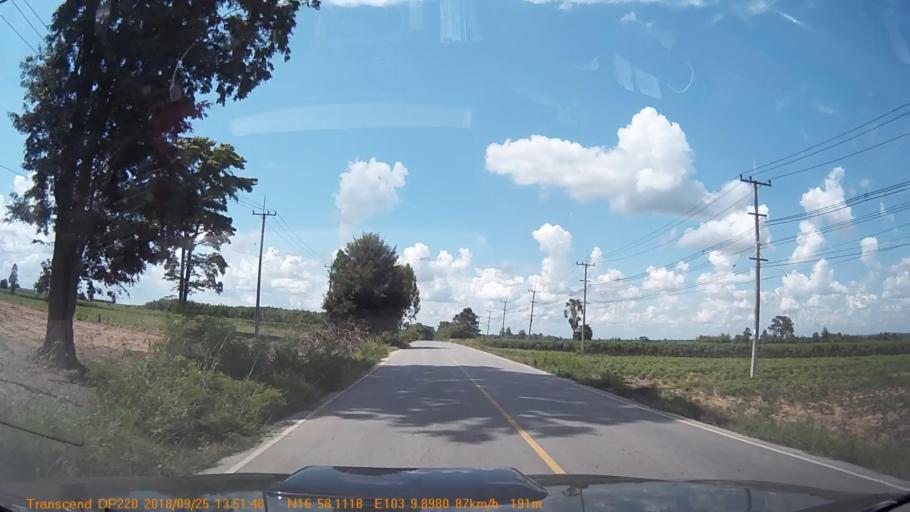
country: TH
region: Changwat Udon Thani
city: Si That
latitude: 16.9687
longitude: 103.1649
